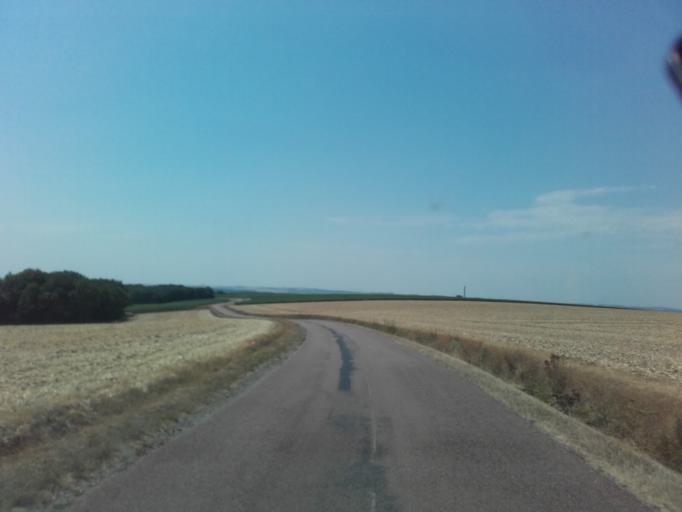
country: FR
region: Bourgogne
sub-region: Departement de l'Yonne
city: Tonnerre
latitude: 47.7862
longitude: 3.9275
